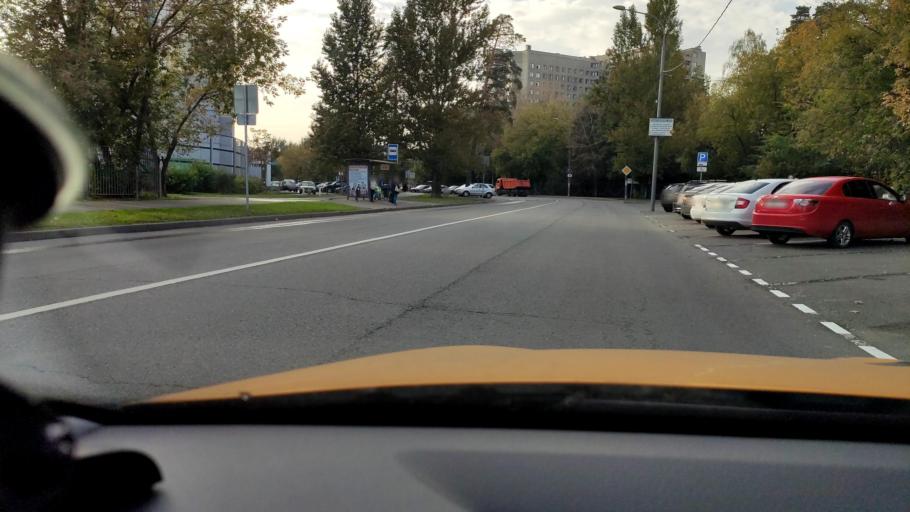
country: RU
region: Moscow
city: Yaroslavskiy
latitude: 55.8865
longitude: 37.7074
